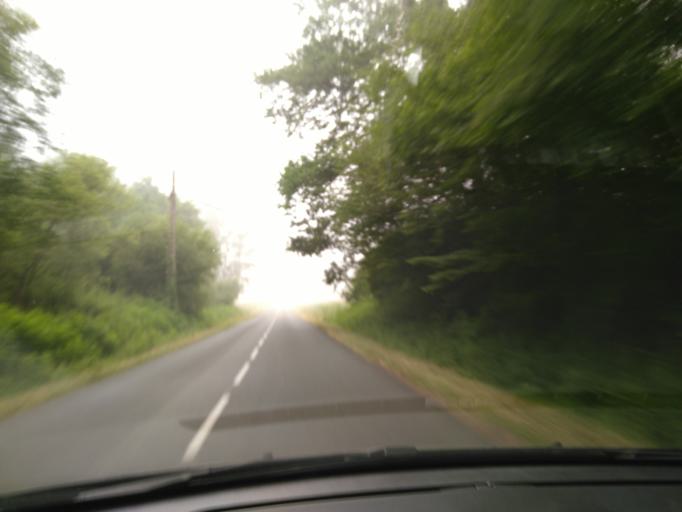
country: FR
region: Aquitaine
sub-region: Departement des Landes
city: Villeneuve-de-Marsan
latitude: 43.8689
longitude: -0.2418
